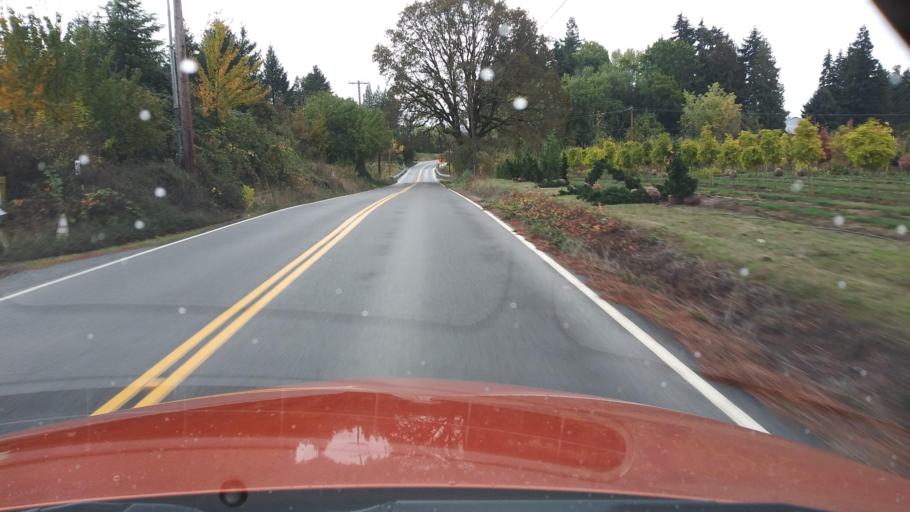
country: US
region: Oregon
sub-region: Washington County
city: Forest Grove
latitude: 45.5313
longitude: -123.0871
